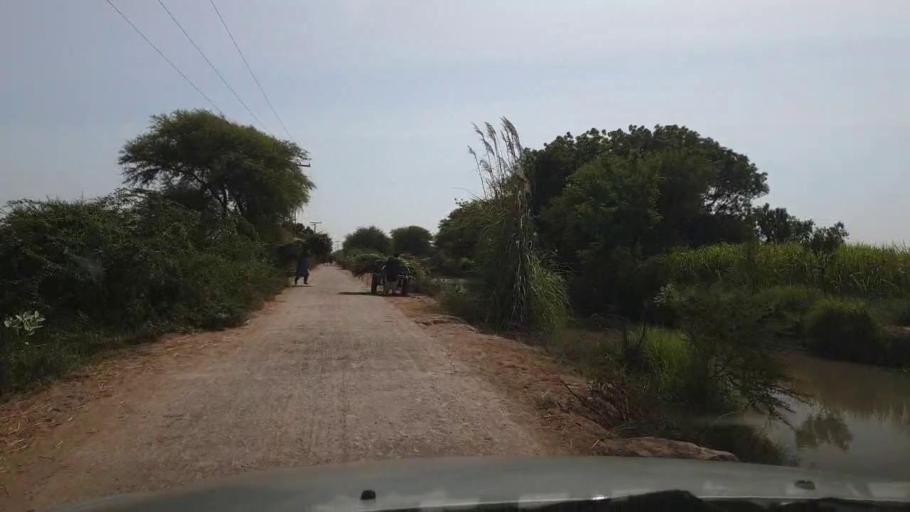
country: PK
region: Sindh
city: Tando Muhammad Khan
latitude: 25.1473
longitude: 68.3953
